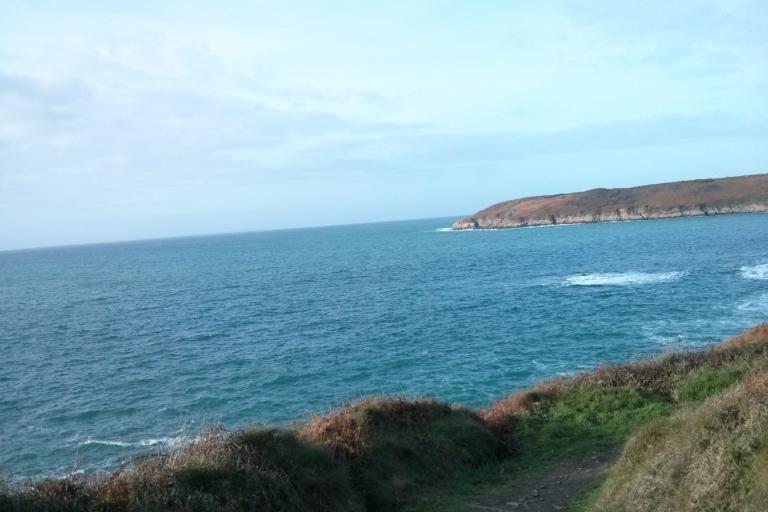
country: FR
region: Brittany
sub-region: Departement du Finistere
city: Le Conquet
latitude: 48.3990
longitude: -4.7739
